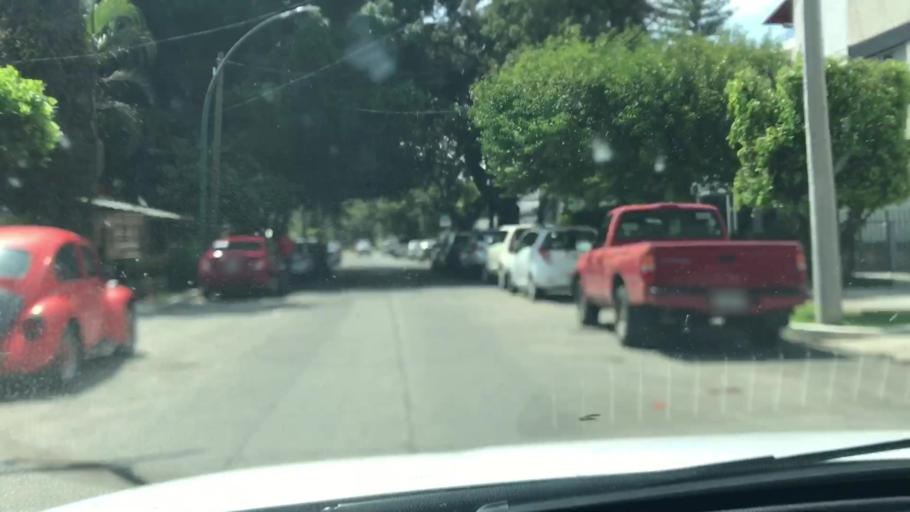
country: MX
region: Jalisco
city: Guadalajara
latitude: 20.6639
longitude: -103.4038
